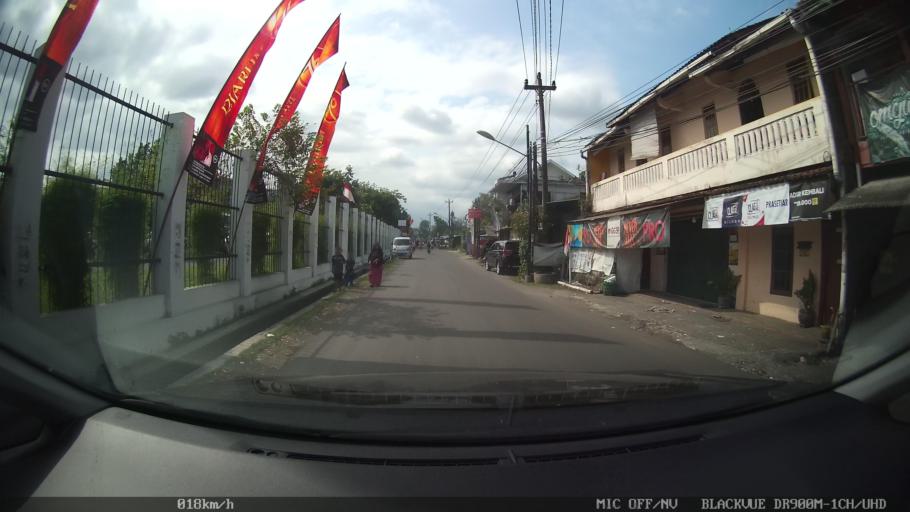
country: ID
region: Daerah Istimewa Yogyakarta
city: Depok
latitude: -7.7527
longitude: 110.4196
